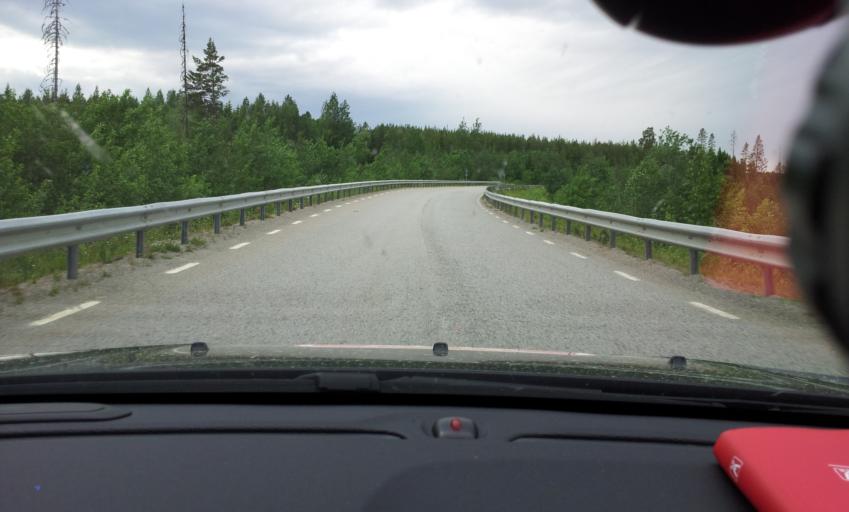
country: SE
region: Jaemtland
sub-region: Bergs Kommun
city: Hoverberg
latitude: 62.6723
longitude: 14.7183
